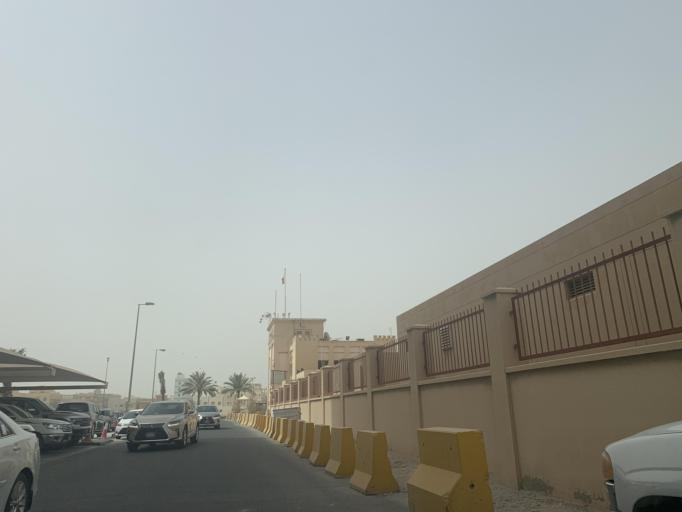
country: BH
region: Manama
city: Jidd Hafs
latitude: 26.2299
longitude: 50.5441
